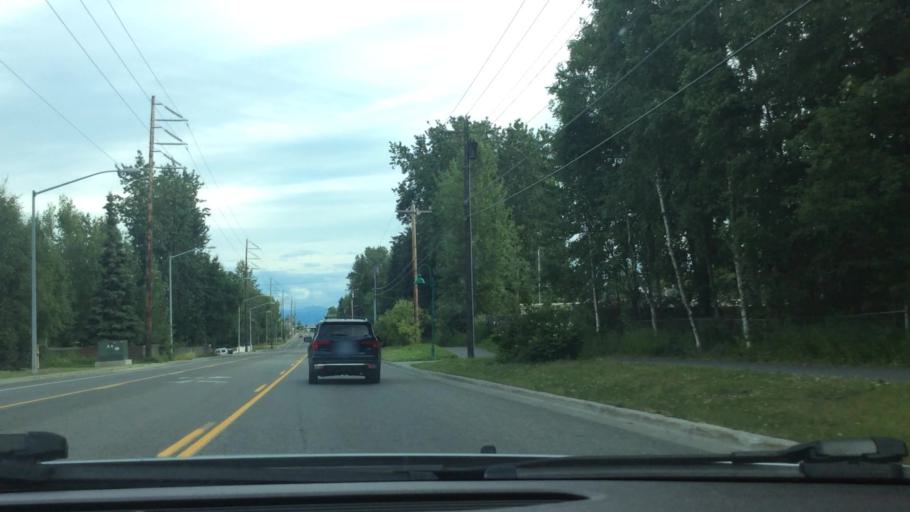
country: US
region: Alaska
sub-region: Anchorage Municipality
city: Anchorage
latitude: 61.1789
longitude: -149.8980
